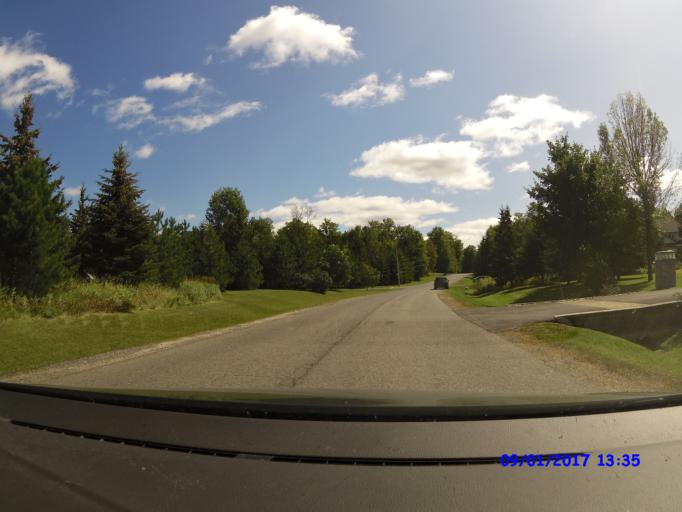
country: CA
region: Ontario
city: Bells Corners
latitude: 45.3557
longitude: -75.9889
